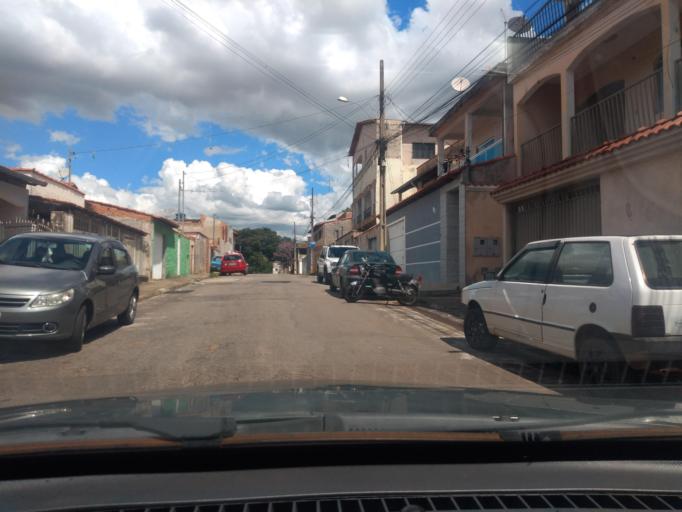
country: BR
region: Minas Gerais
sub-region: Tres Coracoes
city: Tres Coracoes
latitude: -21.6844
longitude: -45.2566
